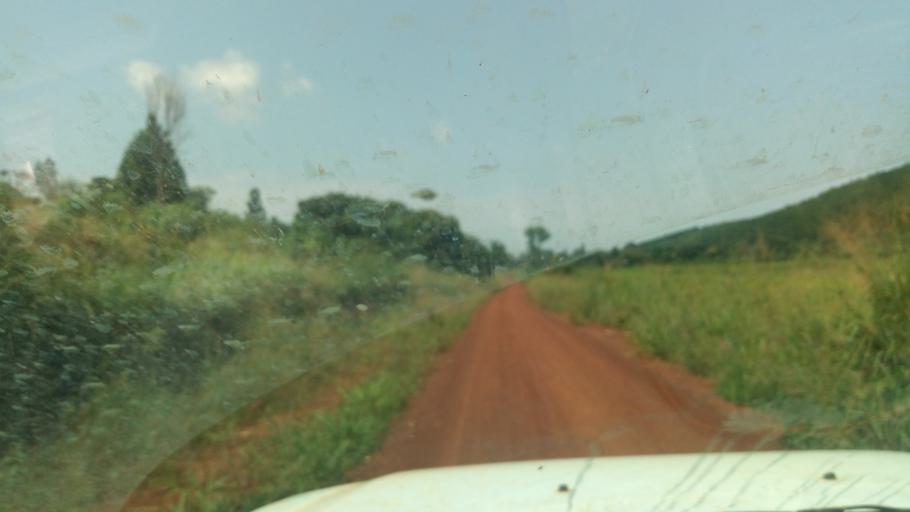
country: UG
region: Western Region
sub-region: Masindi District
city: Masindi
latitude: 1.6470
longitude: 31.8057
